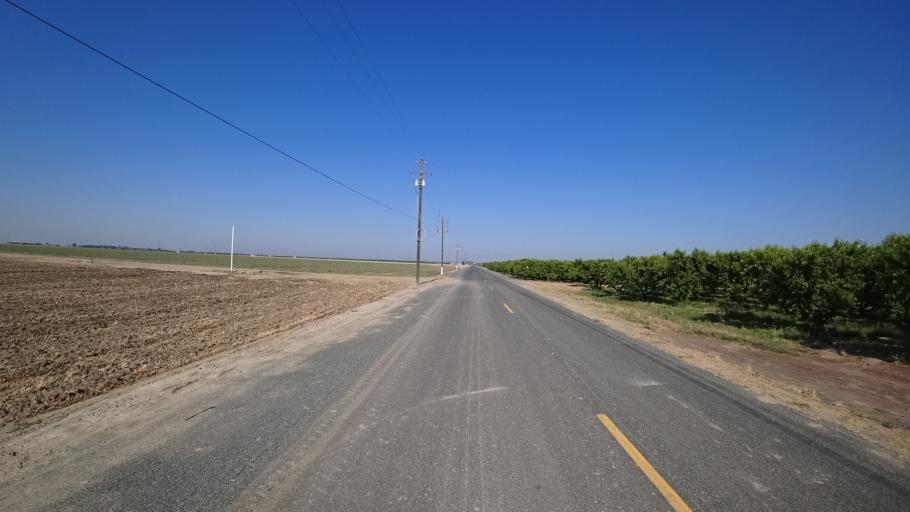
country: US
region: California
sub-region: Kings County
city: Hanford
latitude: 36.3866
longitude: -119.5601
